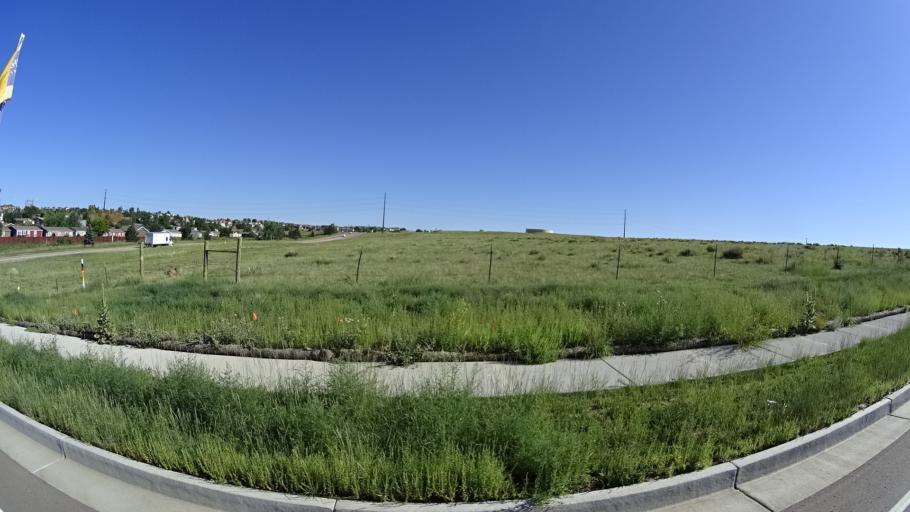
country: US
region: Colorado
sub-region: El Paso County
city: Cimarron Hills
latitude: 38.8971
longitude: -104.6820
